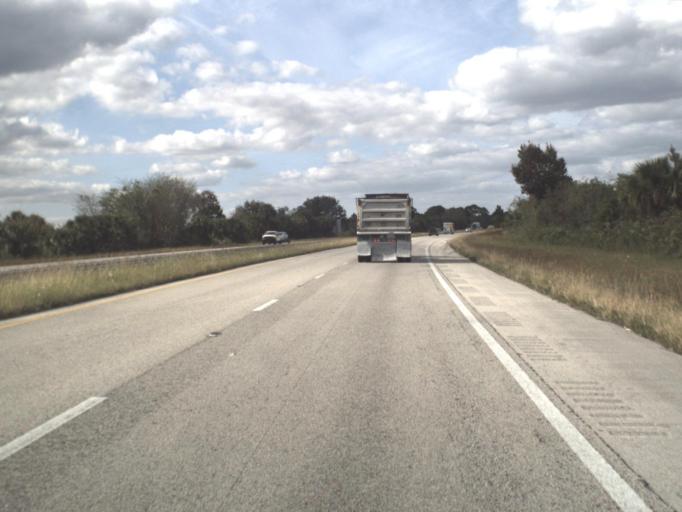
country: US
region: Florida
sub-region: Brevard County
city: Port Saint John
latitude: 28.4142
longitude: -80.8386
